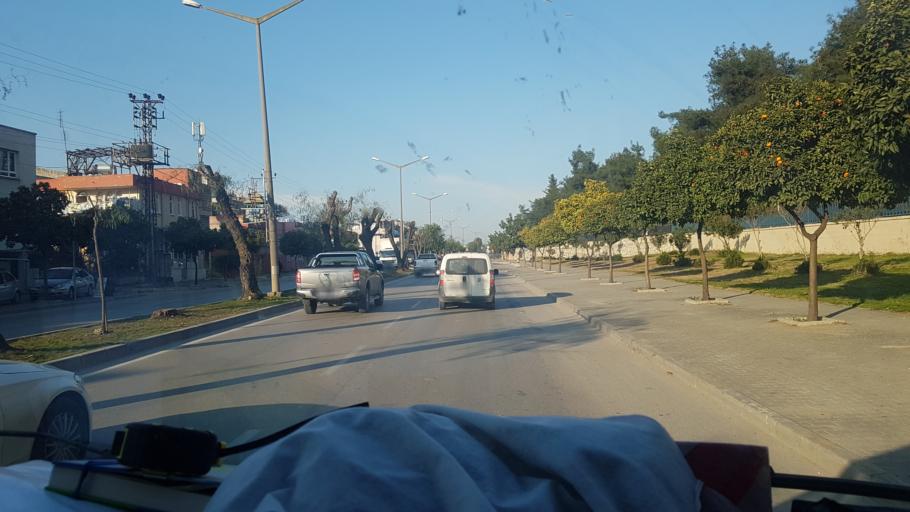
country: TR
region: Adana
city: Adana
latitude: 37.0164
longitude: 35.3401
